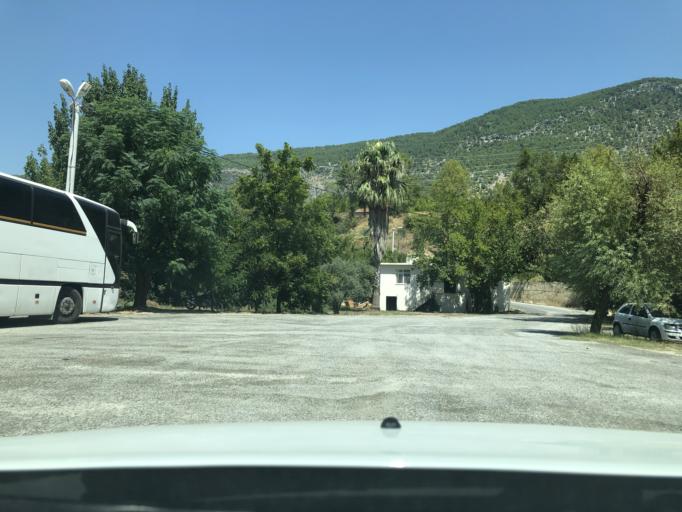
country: TR
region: Antalya
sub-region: Manavgat
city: Manavgat
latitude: 36.8744
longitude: 31.5470
